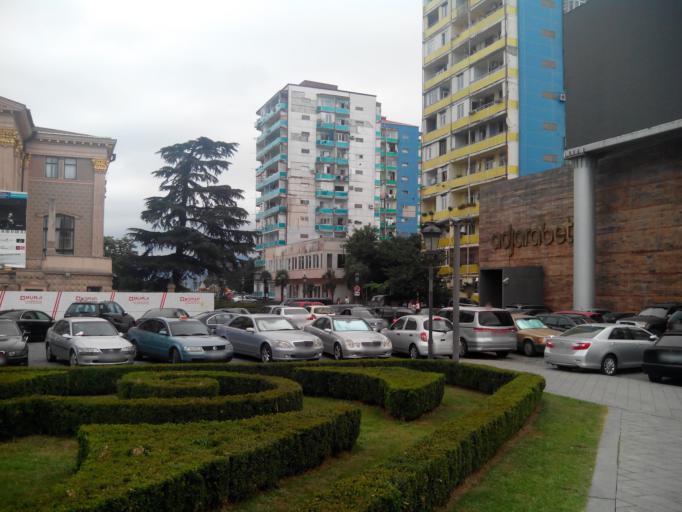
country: GE
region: Ajaria
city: Batumi
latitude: 41.6523
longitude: 41.6376
